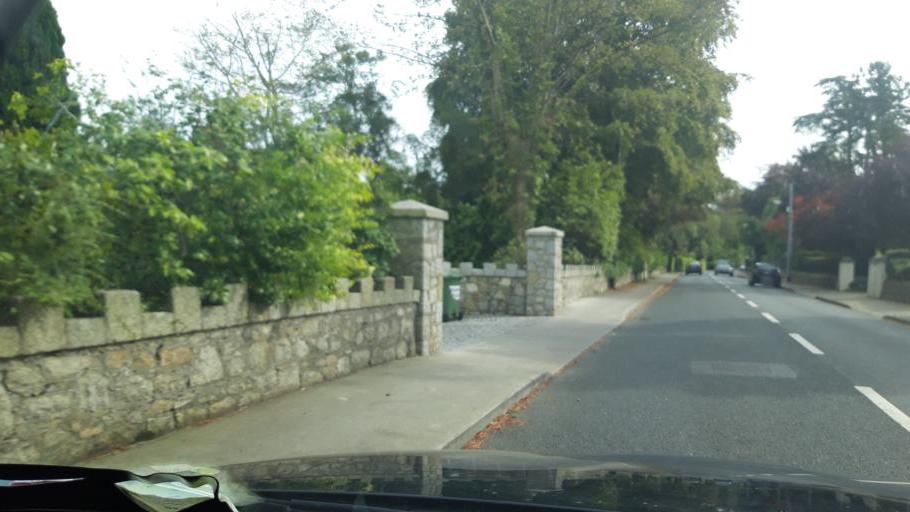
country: IE
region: Leinster
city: Foxrock
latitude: 53.2721
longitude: -6.1877
